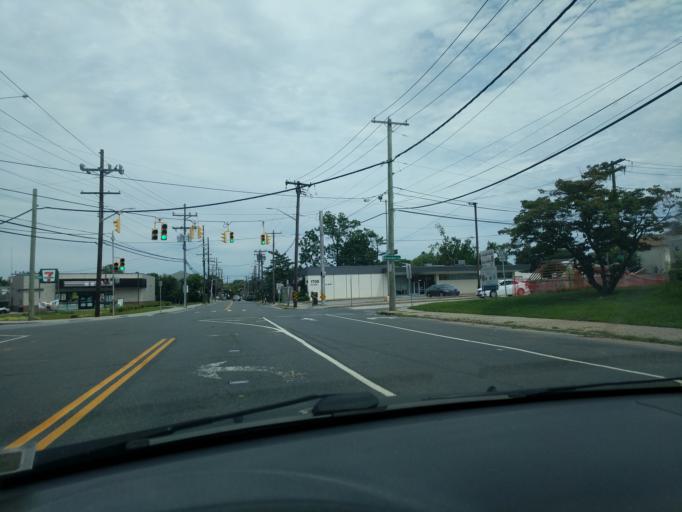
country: US
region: New York
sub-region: Nassau County
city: Hewlett
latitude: 40.6467
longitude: -73.6906
